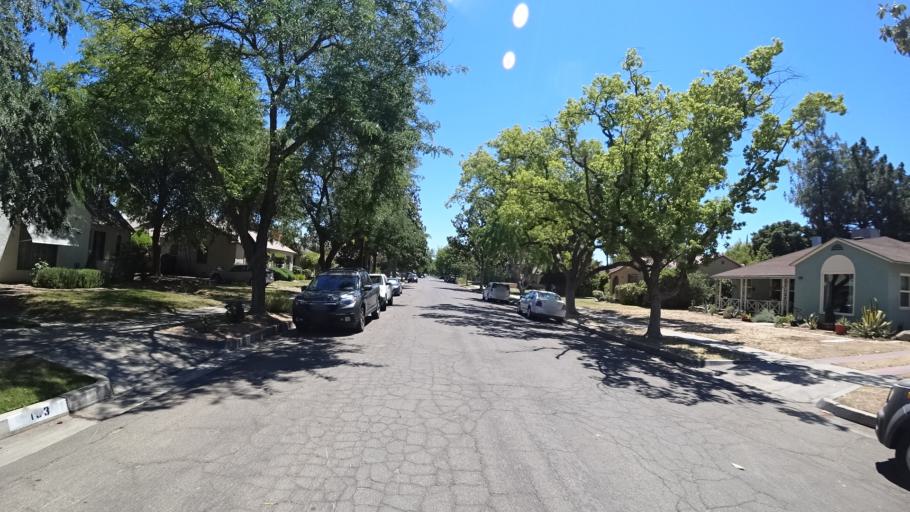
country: US
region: California
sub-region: Fresno County
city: Fresno
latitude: 36.7767
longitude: -119.8100
